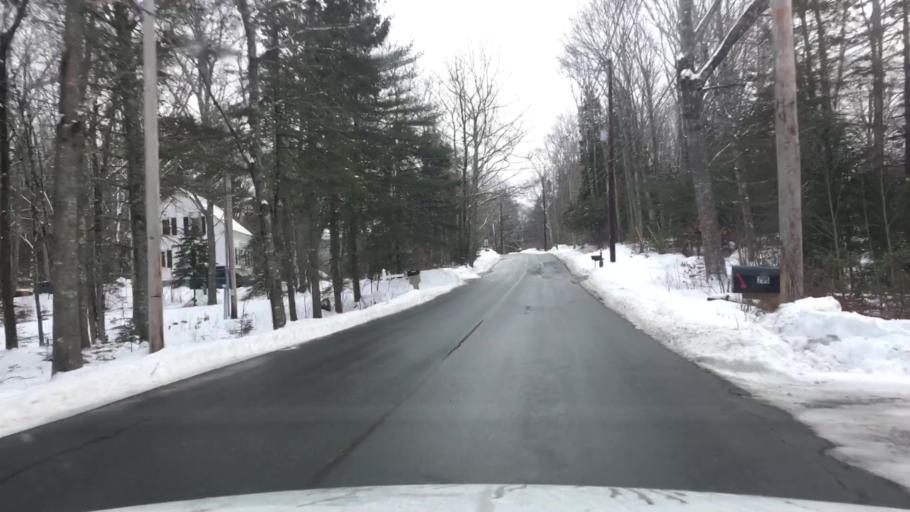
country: US
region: Maine
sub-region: Hancock County
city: Trenton
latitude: 44.4185
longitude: -68.3341
